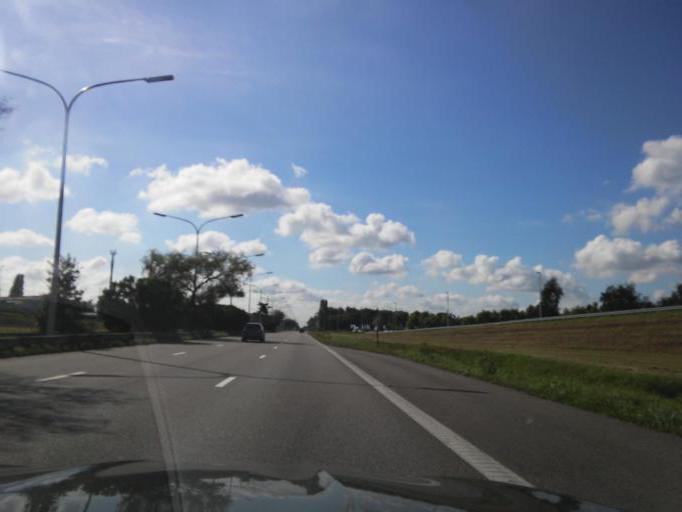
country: BE
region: Flanders
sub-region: Provincie Antwerpen
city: Willebroek
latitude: 51.0490
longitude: 4.3339
